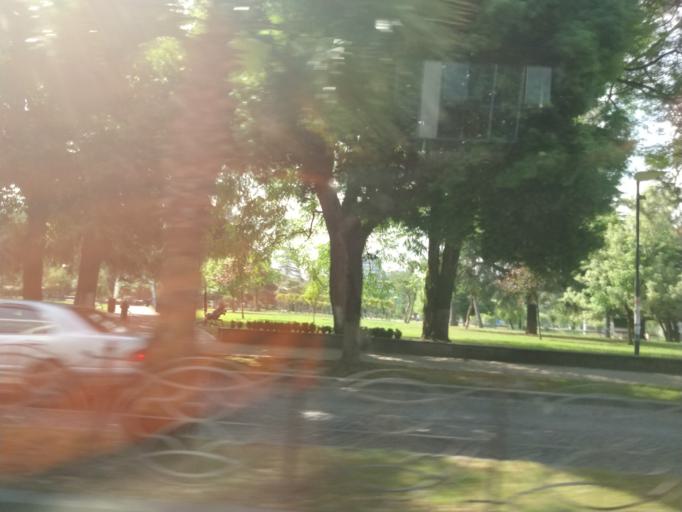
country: GE
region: Ajaria
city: Batumi
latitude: 41.6496
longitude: 41.6278
